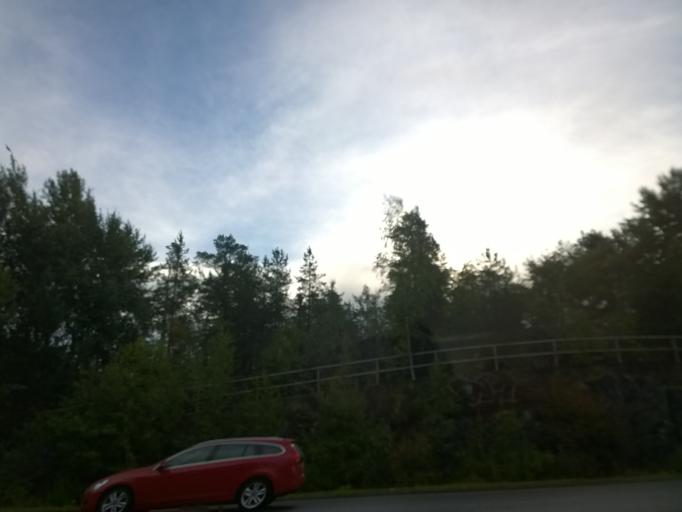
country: FI
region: Pirkanmaa
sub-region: Tampere
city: Tampere
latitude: 61.4686
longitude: 23.8410
